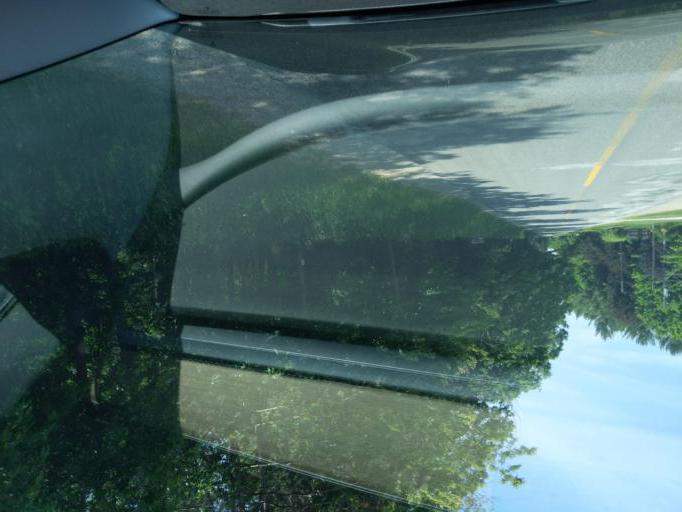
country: US
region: Michigan
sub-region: Muskegon County
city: Montague
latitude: 43.4160
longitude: -86.4164
